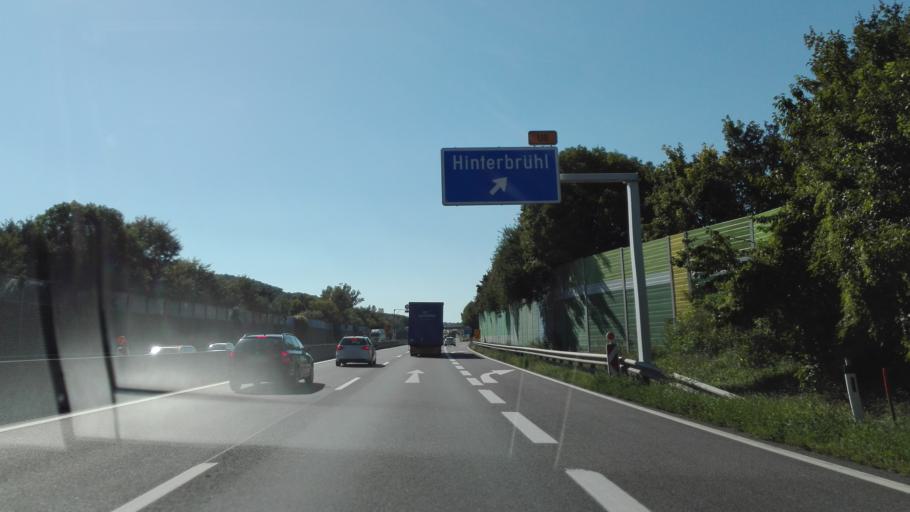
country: AT
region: Lower Austria
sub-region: Politischer Bezirk Modling
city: Gaaden
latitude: 48.0718
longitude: 16.1922
